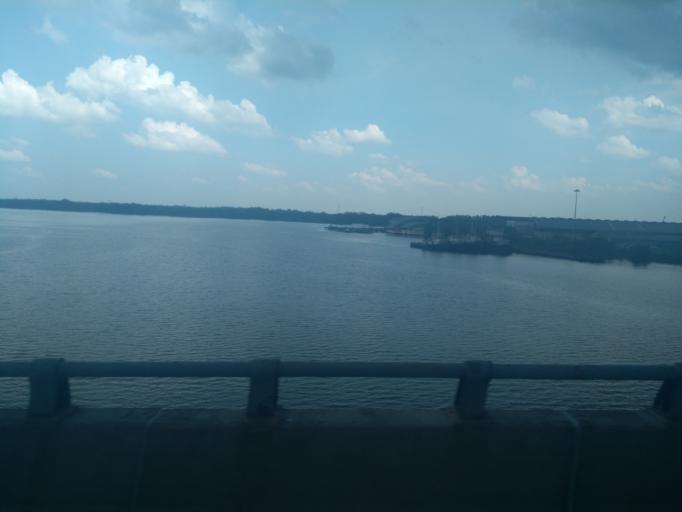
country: MY
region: Sarawak
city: Kuching
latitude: 1.5584
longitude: 110.3962
